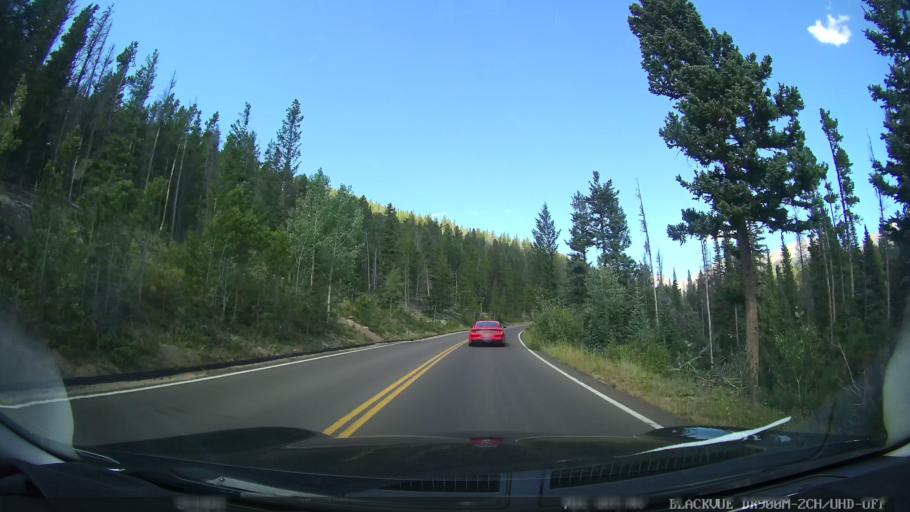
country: US
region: Colorado
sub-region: Larimer County
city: Estes Park
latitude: 40.3965
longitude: -105.6359
